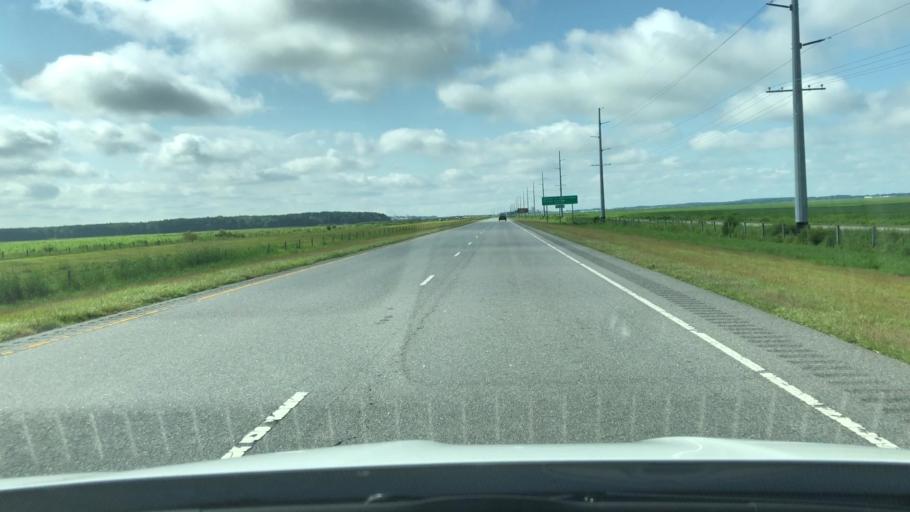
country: US
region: North Carolina
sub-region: Pasquotank County
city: Elizabeth City
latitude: 36.3158
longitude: -76.3083
